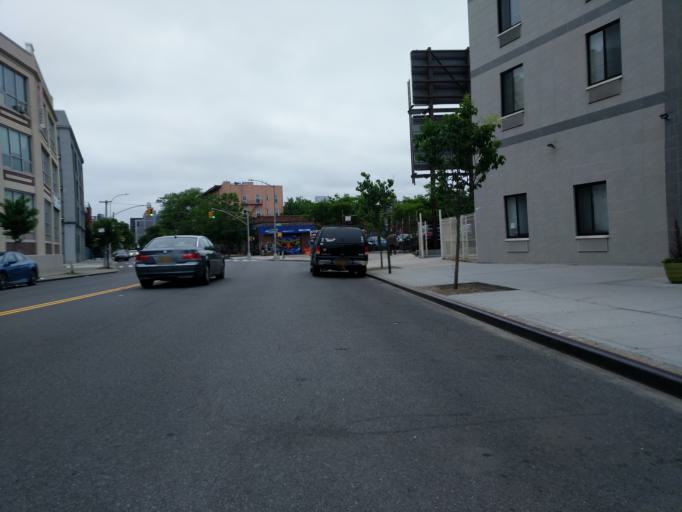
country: US
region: New York
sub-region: Queens County
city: Long Island City
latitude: 40.7494
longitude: -73.9468
